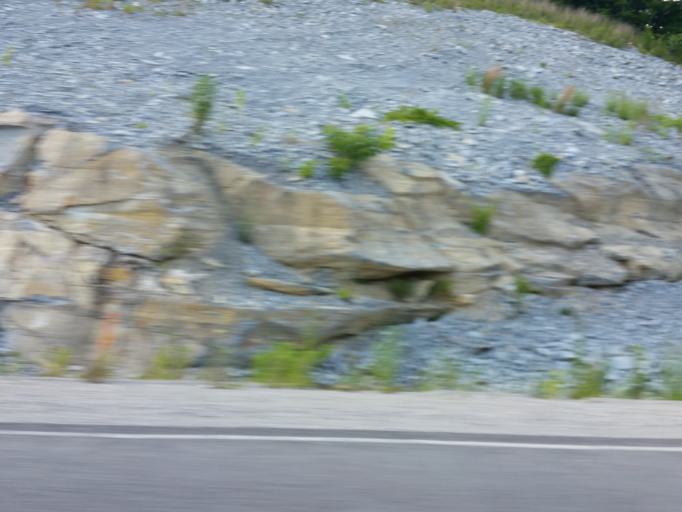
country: US
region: Tennessee
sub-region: Maury County
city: Mount Pleasant
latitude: 35.5647
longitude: -87.3730
